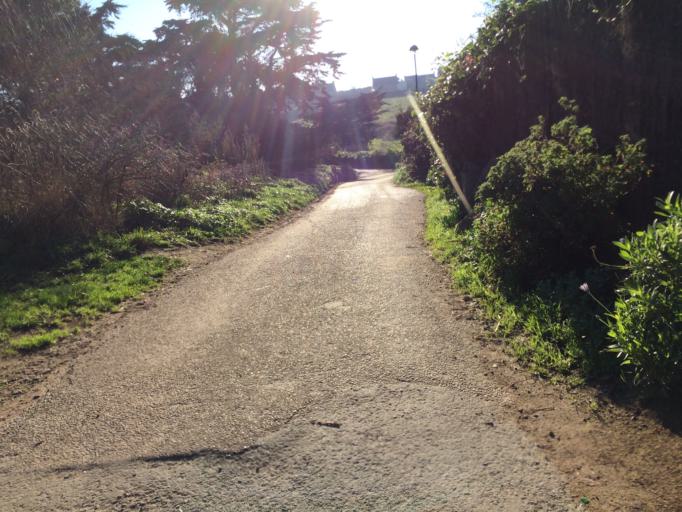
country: FR
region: Brittany
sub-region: Departement des Cotes-d'Armor
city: Ploubazlanec
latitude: 48.8580
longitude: -2.9969
